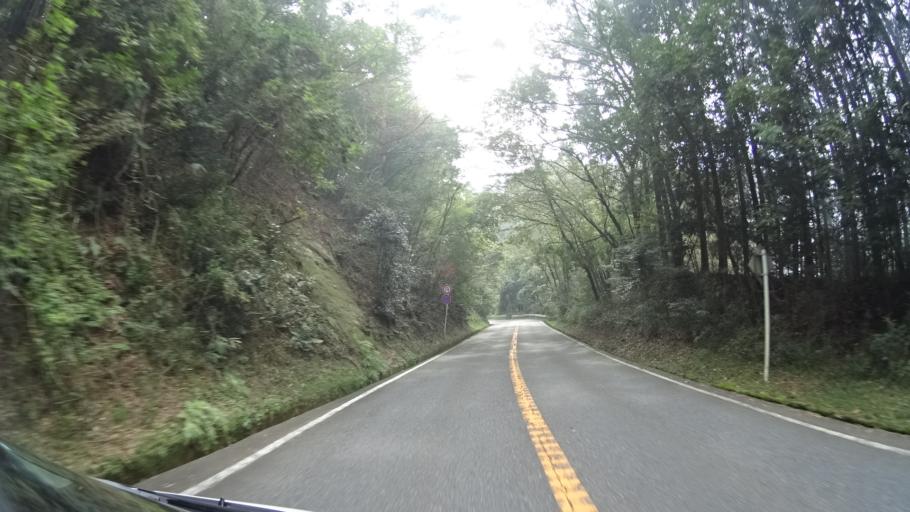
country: JP
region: Shiga Prefecture
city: Otsu-shi
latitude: 35.0407
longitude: 135.8240
